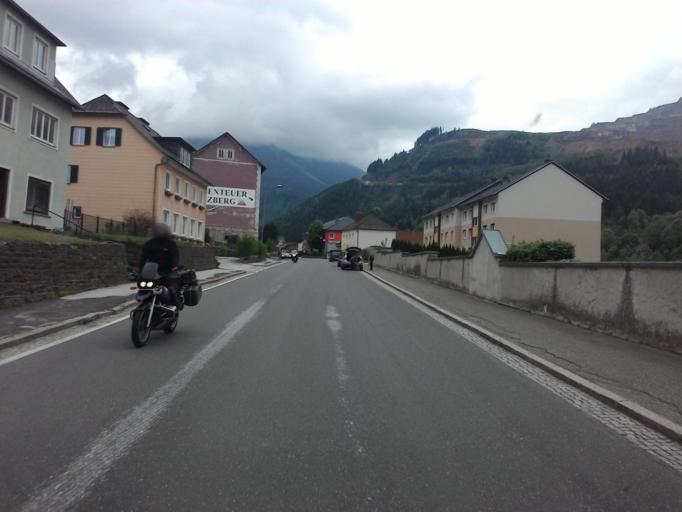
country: AT
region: Styria
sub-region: Politischer Bezirk Leoben
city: Eisenerz
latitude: 47.5414
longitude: 14.8940
